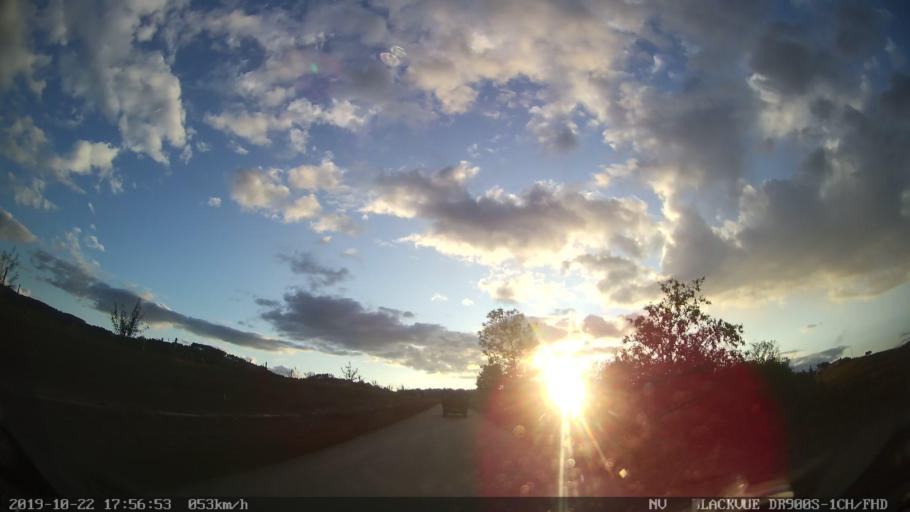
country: PT
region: Vila Real
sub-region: Sabrosa
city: Sabrosa
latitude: 41.2550
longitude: -7.5870
